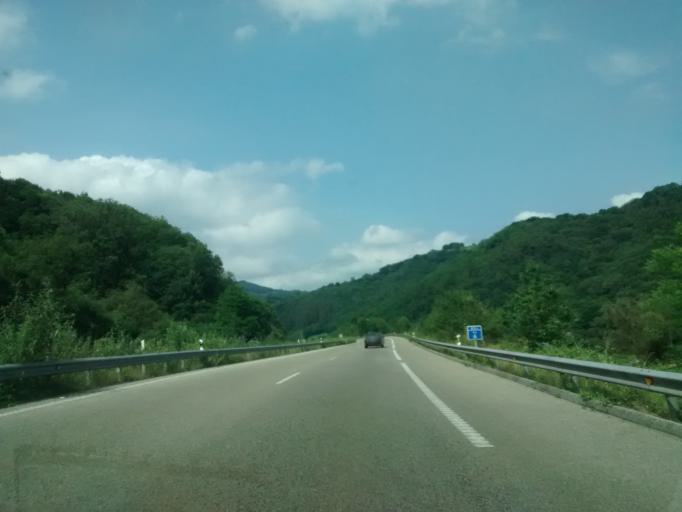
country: ES
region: Asturias
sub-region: Province of Asturias
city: Mieres
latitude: 43.3062
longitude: -5.7486
